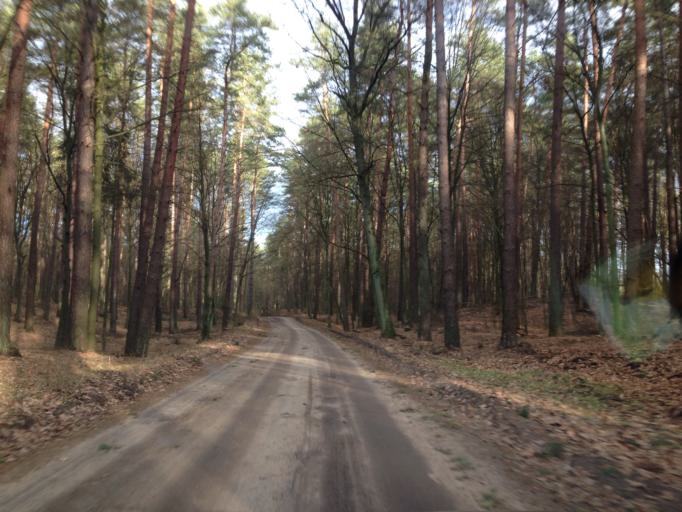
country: PL
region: Kujawsko-Pomorskie
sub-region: Powiat brodnicki
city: Gorzno
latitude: 53.2030
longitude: 19.6763
